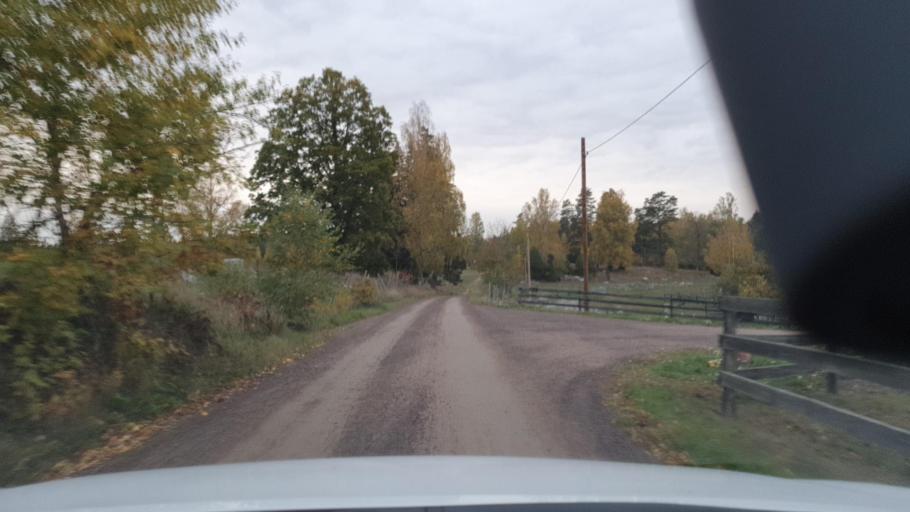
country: SE
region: Kalmar
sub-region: Hultsfreds Kommun
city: Malilla
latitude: 57.3153
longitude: 15.8141
